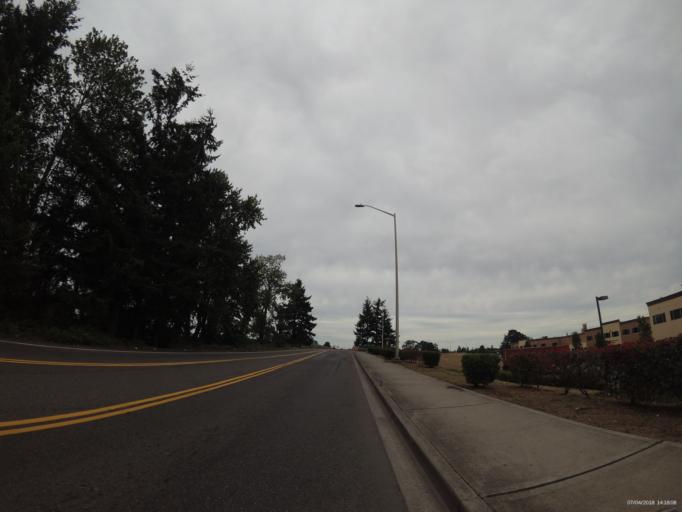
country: US
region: Washington
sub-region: Pierce County
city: McChord Air Force Base
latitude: 47.1580
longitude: -122.4835
